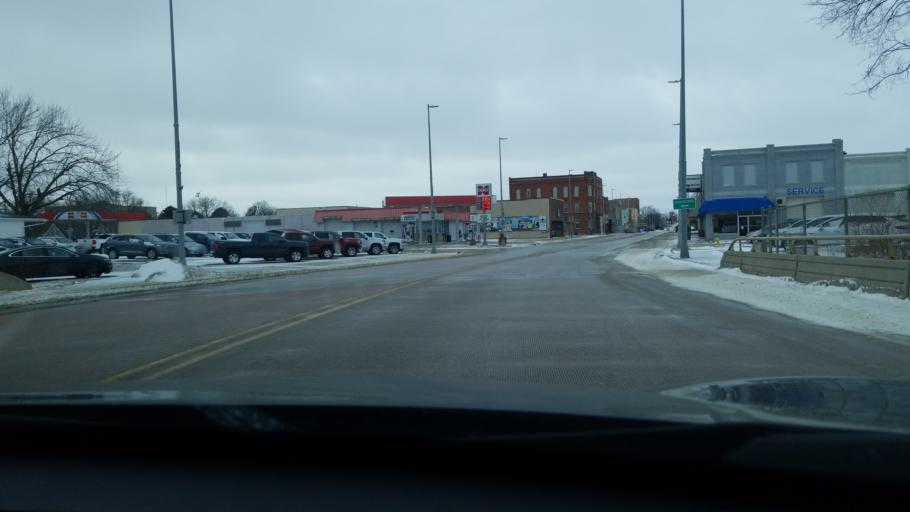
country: US
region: Iowa
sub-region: Lyon County
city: Rock Rapids
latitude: 43.4319
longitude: -96.1648
